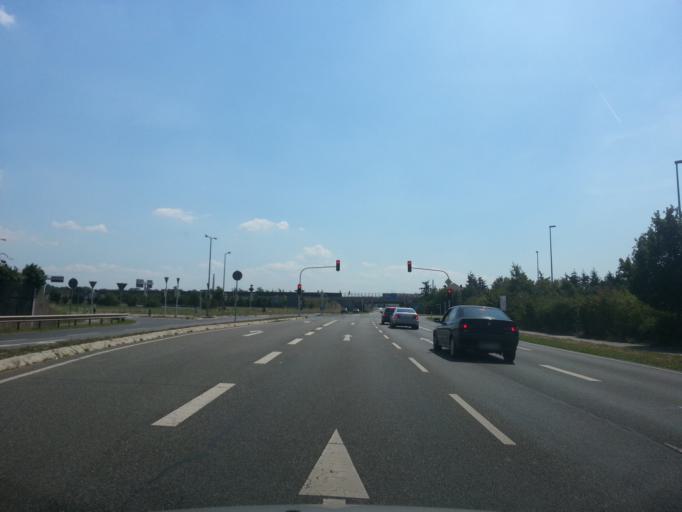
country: DE
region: Hesse
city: Lampertheim
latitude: 49.5559
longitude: 8.4466
